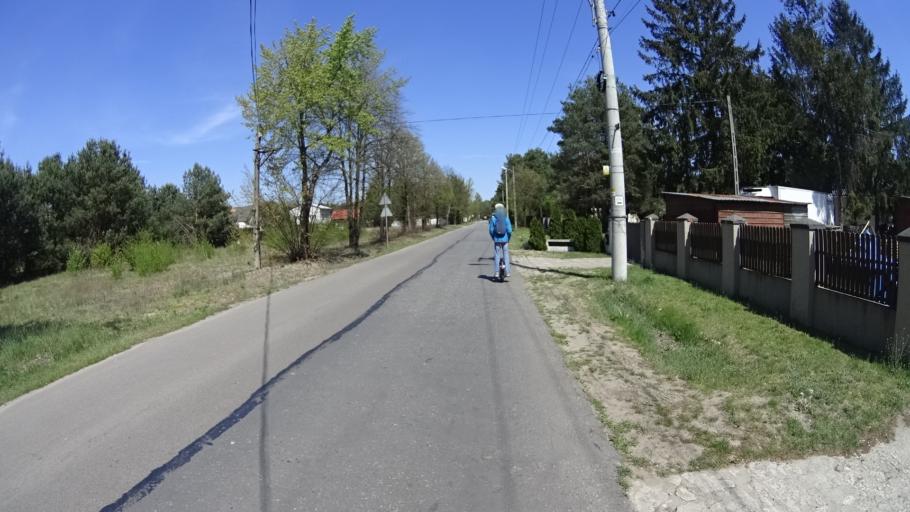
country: PL
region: Masovian Voivodeship
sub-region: Powiat warszawski zachodni
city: Truskaw
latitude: 52.2806
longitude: 20.7430
